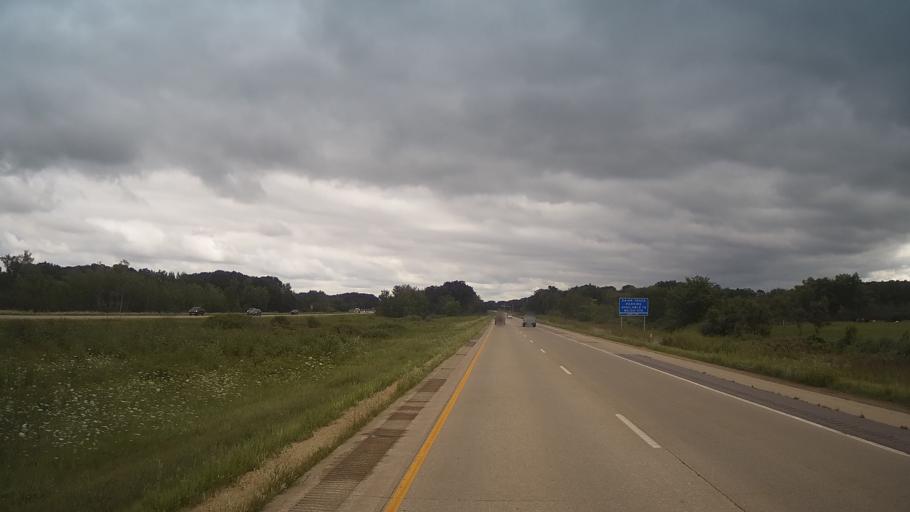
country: US
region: Wisconsin
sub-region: Monroe County
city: Sparta
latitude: 43.9050
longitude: -90.8954
